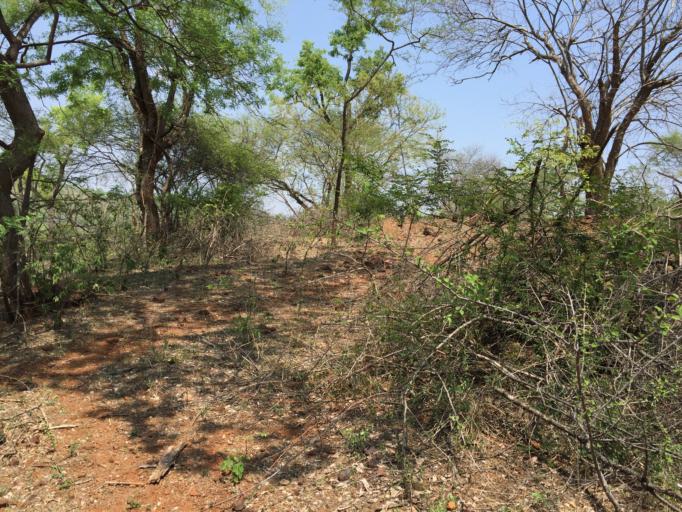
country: IN
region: Karnataka
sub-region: Chamrajnagar
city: Kollegal
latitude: 12.3006
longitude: 77.3031
